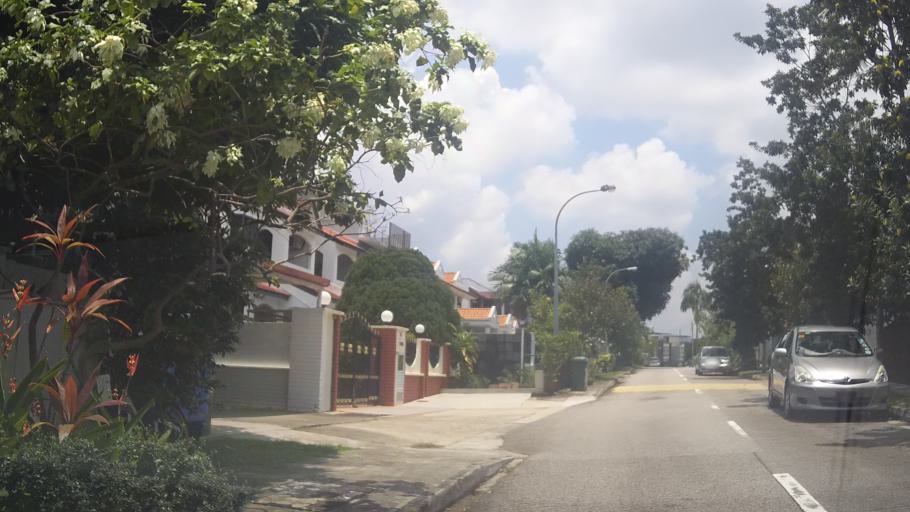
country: SG
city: Singapore
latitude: 1.3606
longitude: 103.8714
